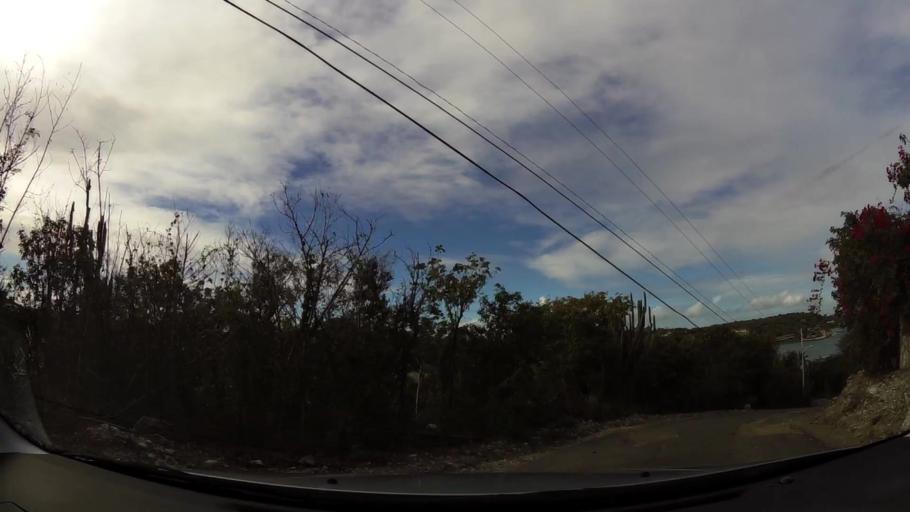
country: AG
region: Saint Peter
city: Parham
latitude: 17.0992
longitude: -61.6873
